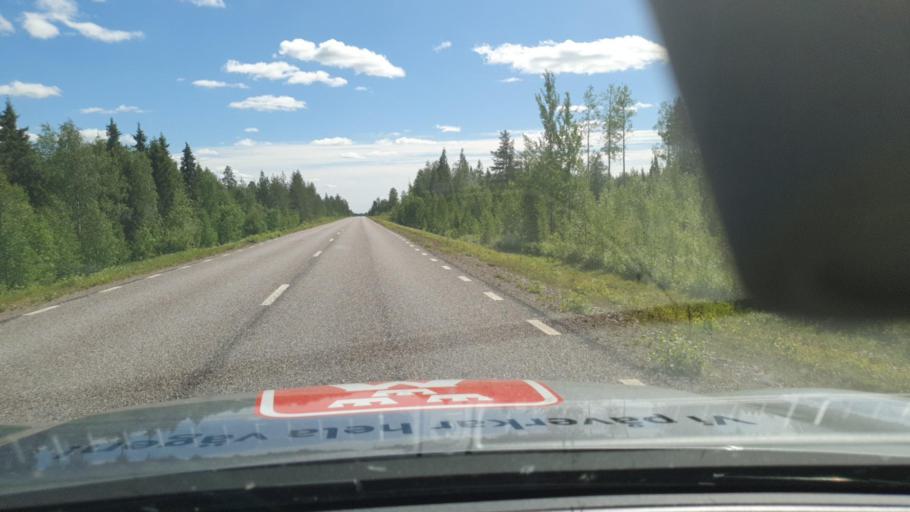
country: SE
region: Norrbotten
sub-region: Pajala Kommun
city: Pajala
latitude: 67.1538
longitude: 23.5551
